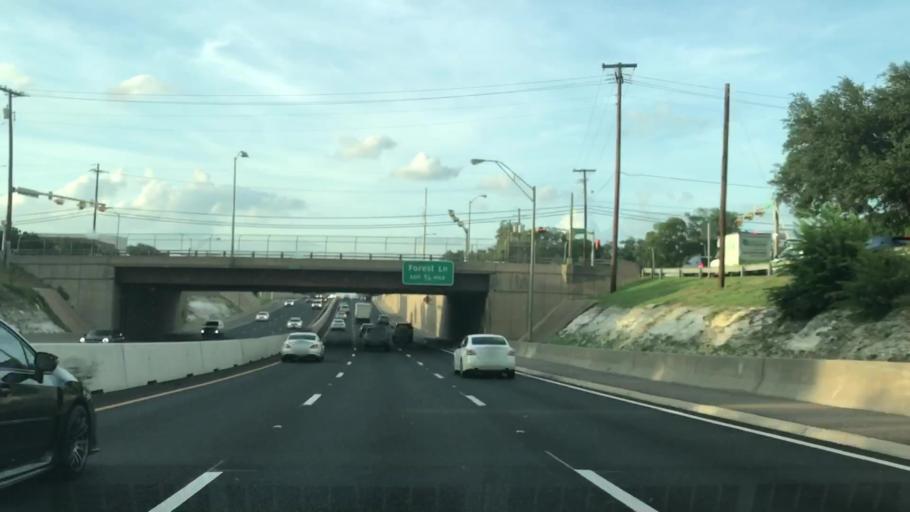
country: US
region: Texas
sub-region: Dallas County
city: University Park
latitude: 32.8942
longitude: -96.8090
